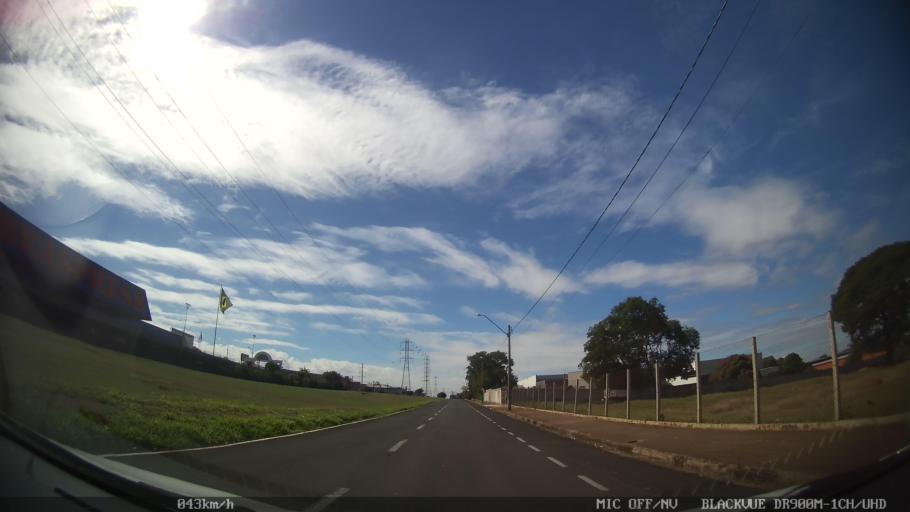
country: BR
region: Sao Paulo
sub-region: Sao Jose Do Rio Preto
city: Sao Jose do Rio Preto
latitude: -20.8389
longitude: -49.3570
